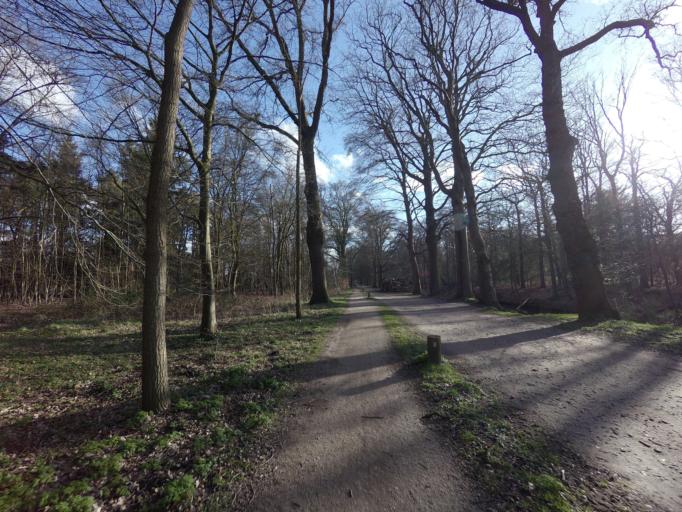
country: NL
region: North Holland
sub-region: Gemeente Wijdemeren
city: Nieuw-Loosdrecht
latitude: 52.2320
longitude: 5.1419
